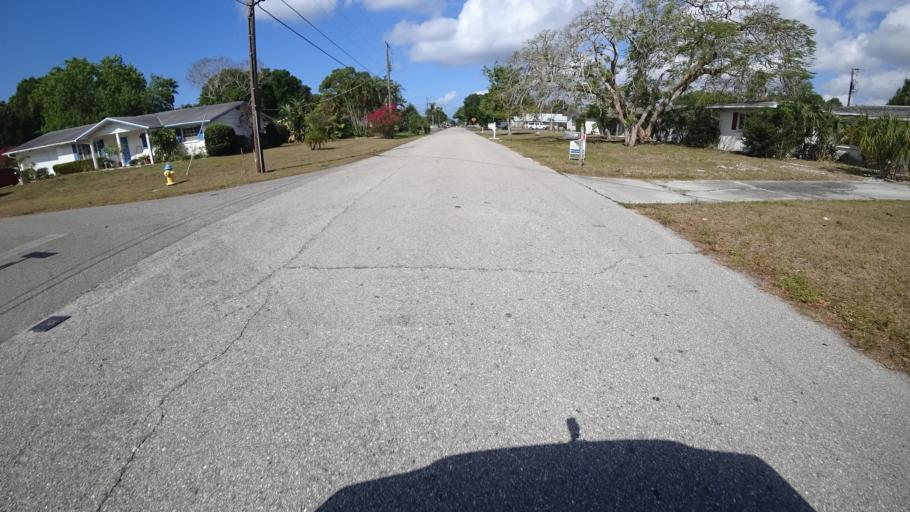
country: US
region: Florida
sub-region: Manatee County
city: Whitfield
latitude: 27.4224
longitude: -82.5650
